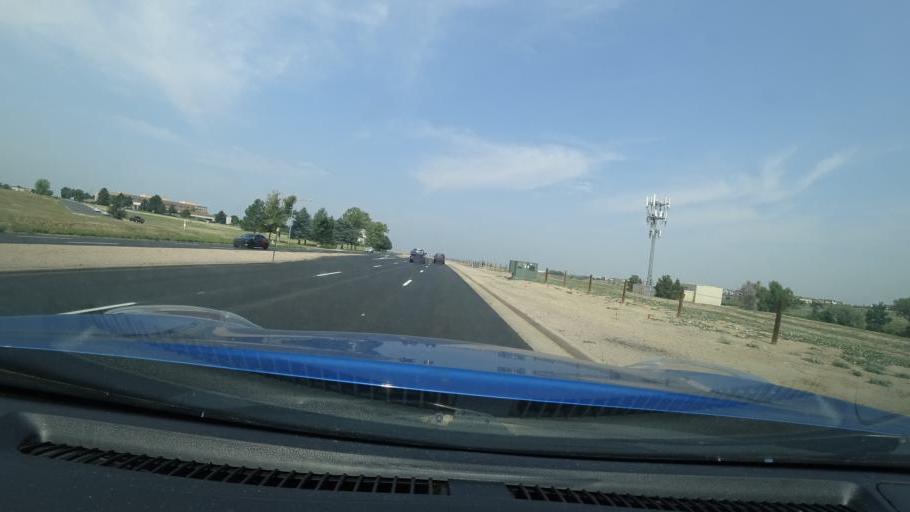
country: US
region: Colorado
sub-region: Adams County
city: Aurora
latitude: 39.7050
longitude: -104.7791
